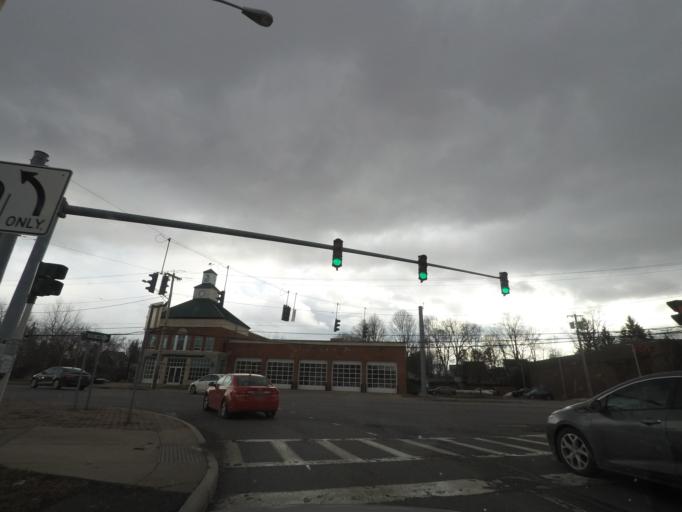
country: US
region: New York
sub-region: Onondaga County
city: East Syracuse
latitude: 43.0350
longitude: -76.0656
